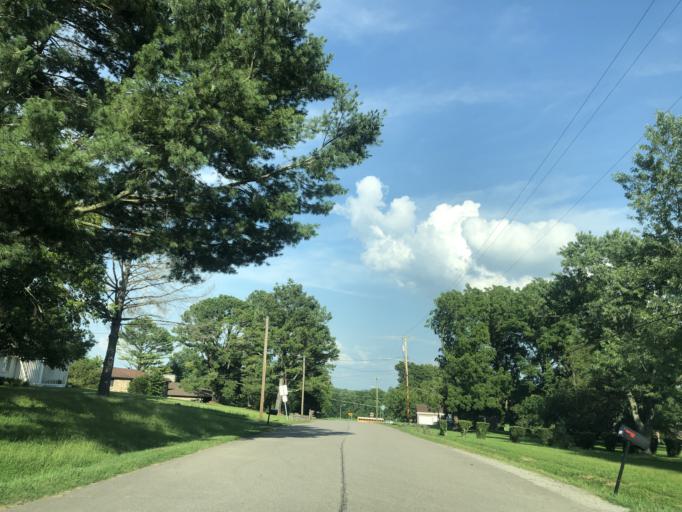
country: US
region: Tennessee
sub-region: Davidson County
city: Nashville
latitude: 36.2360
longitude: -86.8333
